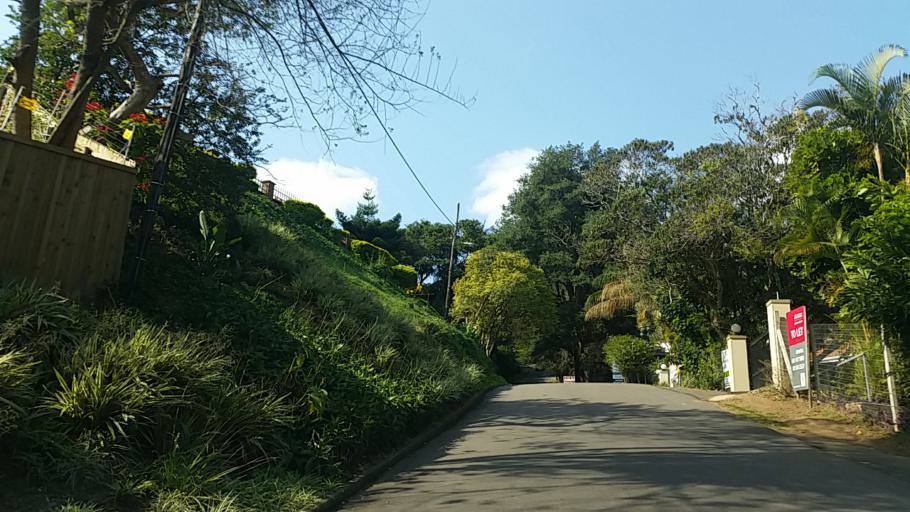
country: ZA
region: KwaZulu-Natal
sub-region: eThekwini Metropolitan Municipality
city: Berea
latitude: -29.8331
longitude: 30.9181
